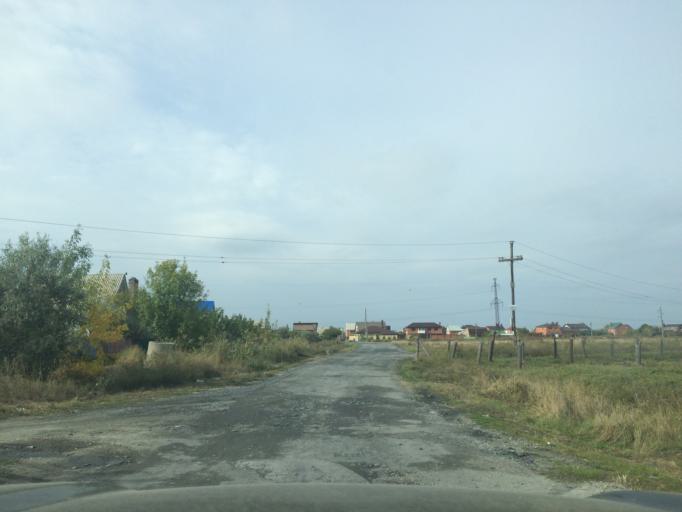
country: RU
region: Rostov
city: Kalinin
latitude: 47.1722
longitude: 39.5505
